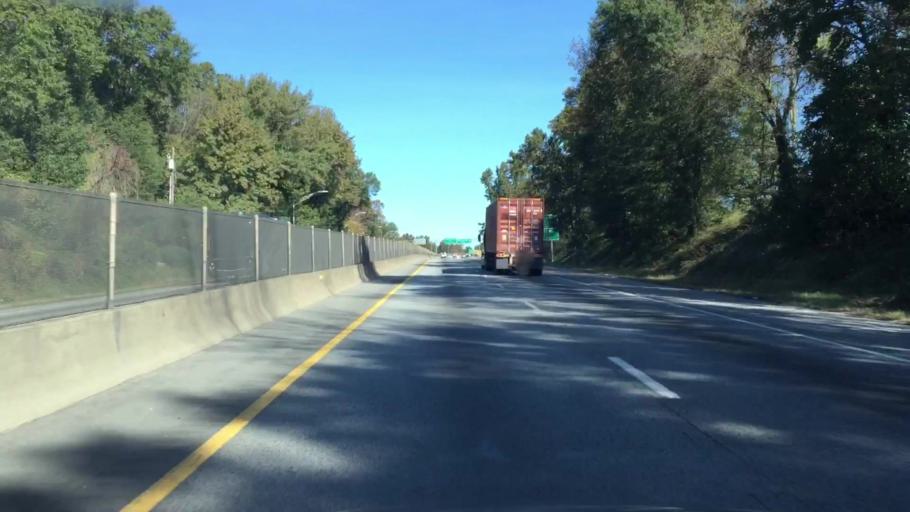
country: US
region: North Carolina
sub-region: Guilford County
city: Greensboro
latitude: 36.0583
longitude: -79.7679
